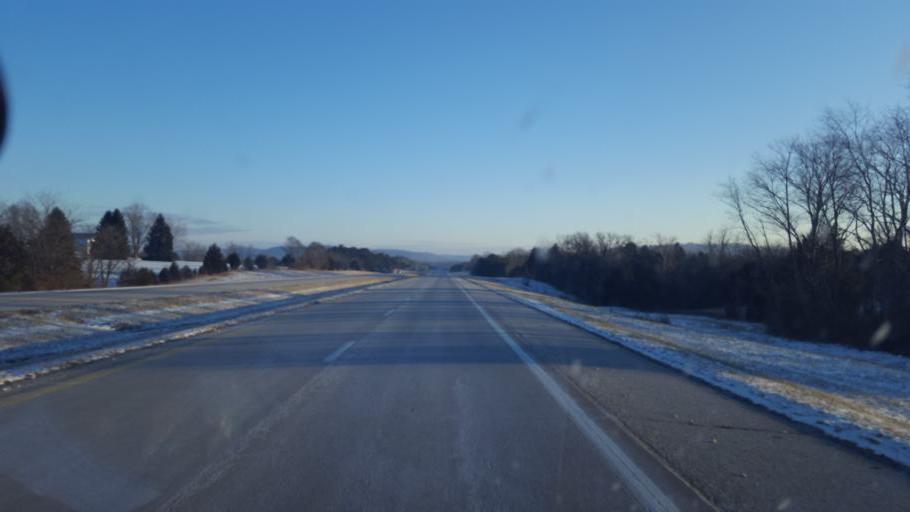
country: US
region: Ohio
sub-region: Adams County
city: Peebles
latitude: 38.9604
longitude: -83.3578
